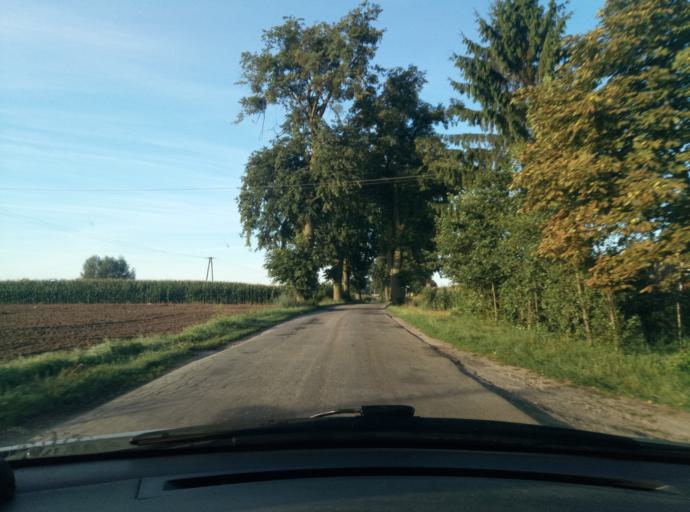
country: PL
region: Kujawsko-Pomorskie
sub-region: Powiat brodnicki
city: Jablonowo Pomorskie
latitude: 53.4173
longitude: 19.1801
